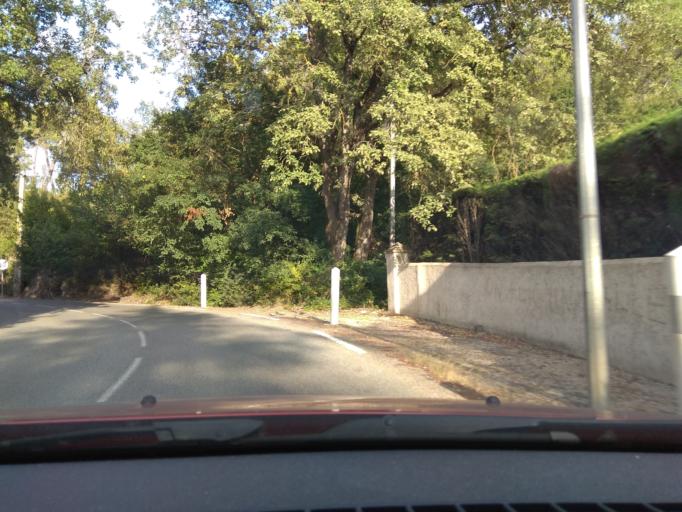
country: FR
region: Provence-Alpes-Cote d'Azur
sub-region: Departement des Alpes-Maritimes
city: Le Rouret
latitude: 43.6785
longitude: 7.0471
